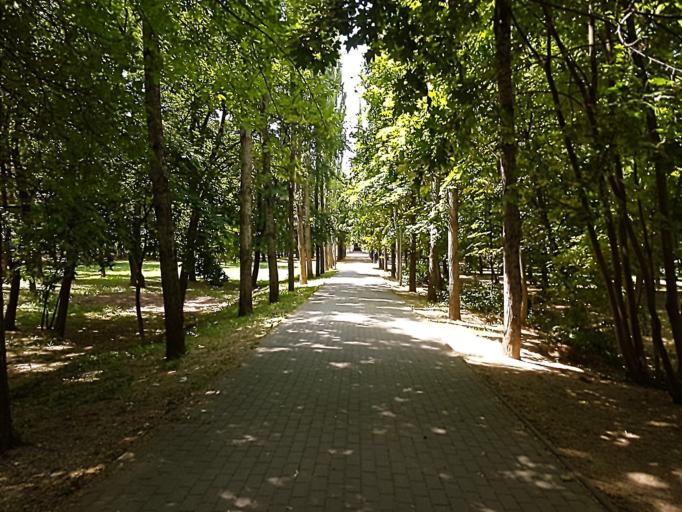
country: HU
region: Pest
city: Solymar
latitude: 47.5619
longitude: 18.9471
